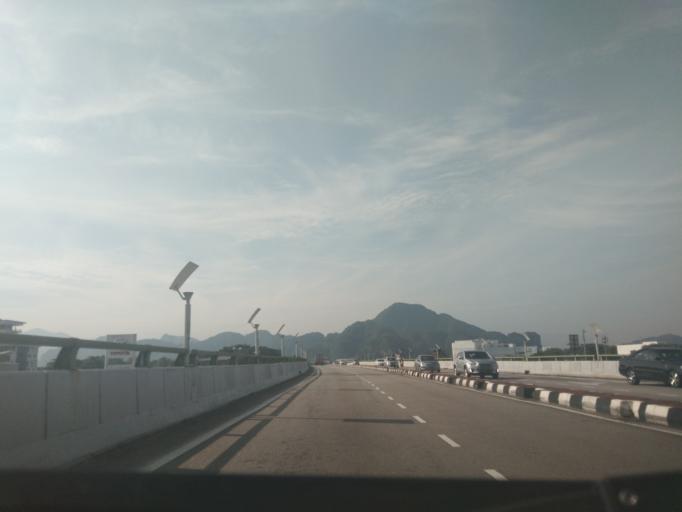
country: MY
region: Perak
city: Ipoh
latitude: 4.5799
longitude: 101.1045
